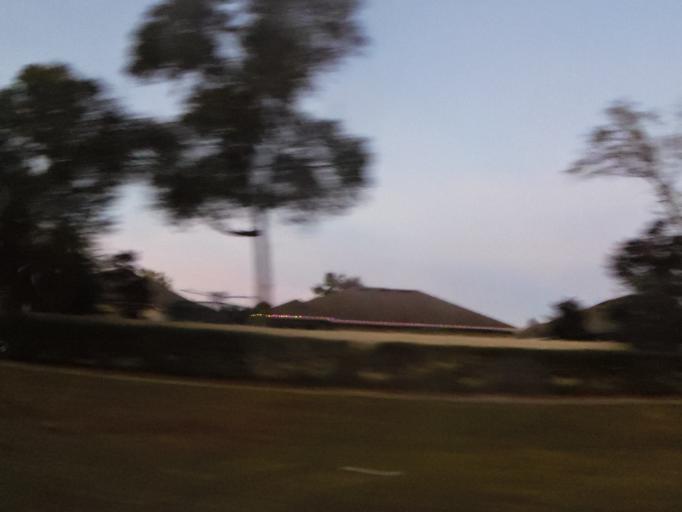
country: US
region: Florida
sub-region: Saint Johns County
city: Saint Augustine Shores
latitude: 29.8151
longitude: -81.3426
